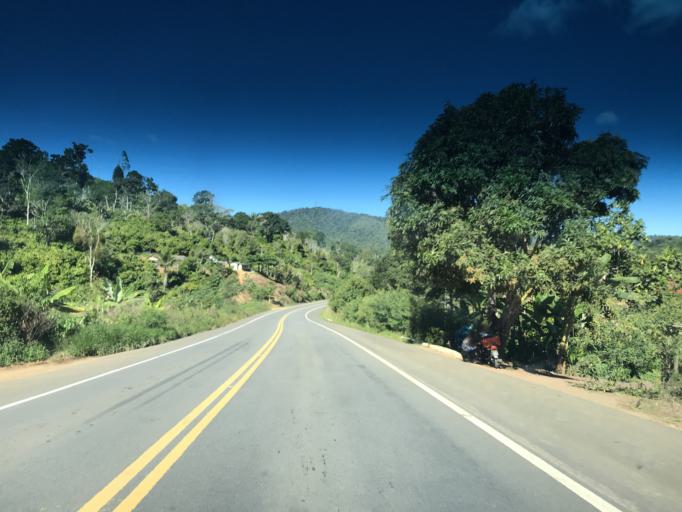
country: BR
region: Bahia
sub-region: Gandu
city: Gandu
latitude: -13.8841
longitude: -39.4857
